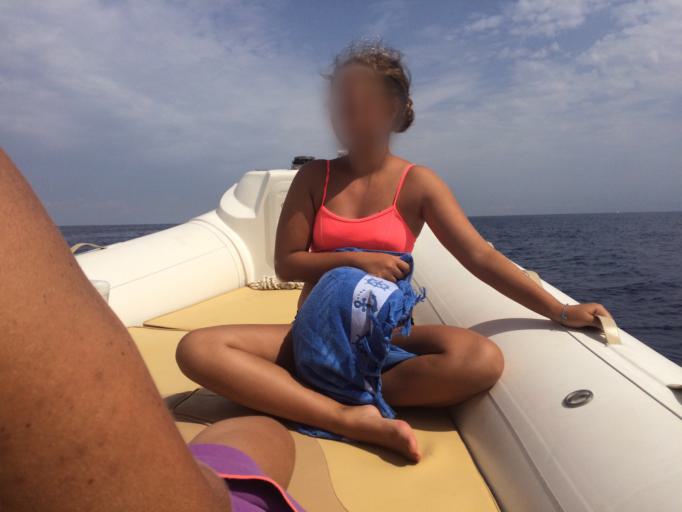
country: IT
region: Tuscany
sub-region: Provincia di Livorno
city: Capraia Isola
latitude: 43.0509
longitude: 9.7945
